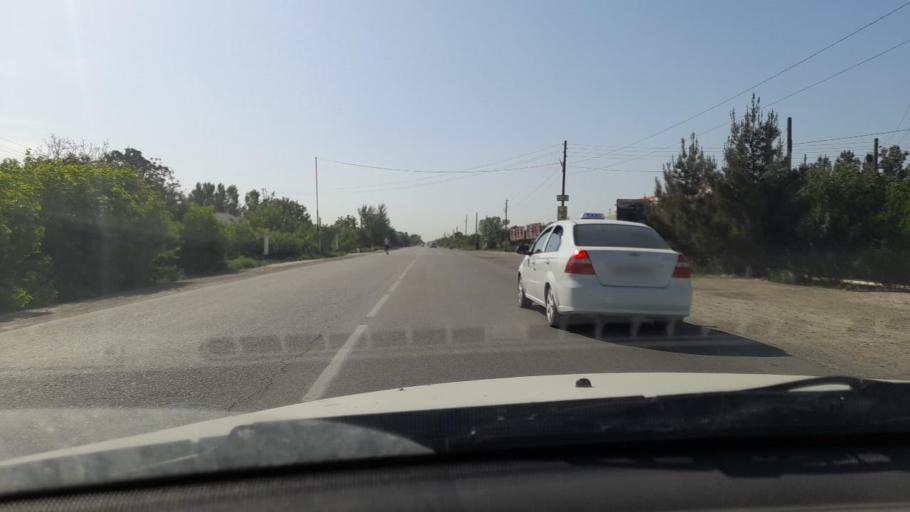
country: UZ
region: Bukhara
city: Romiton
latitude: 39.9058
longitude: 64.4010
